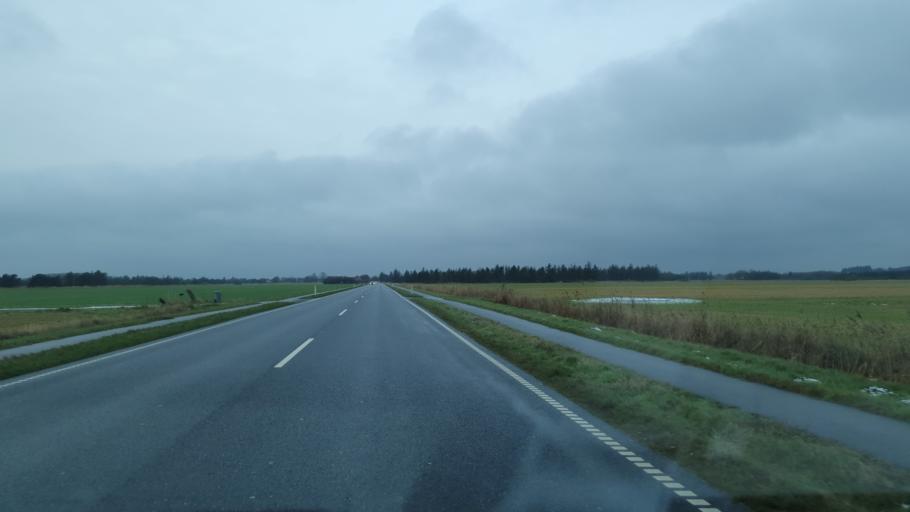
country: DK
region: North Denmark
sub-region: Jammerbugt Kommune
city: Fjerritslev
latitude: 57.0909
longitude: 9.1933
